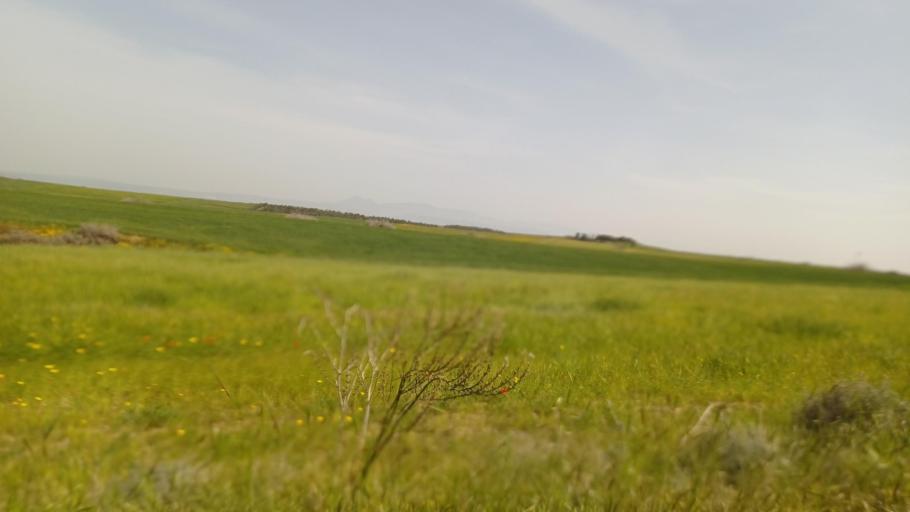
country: CY
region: Lefkosia
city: Astromeritis
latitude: 35.0983
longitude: 32.9612
